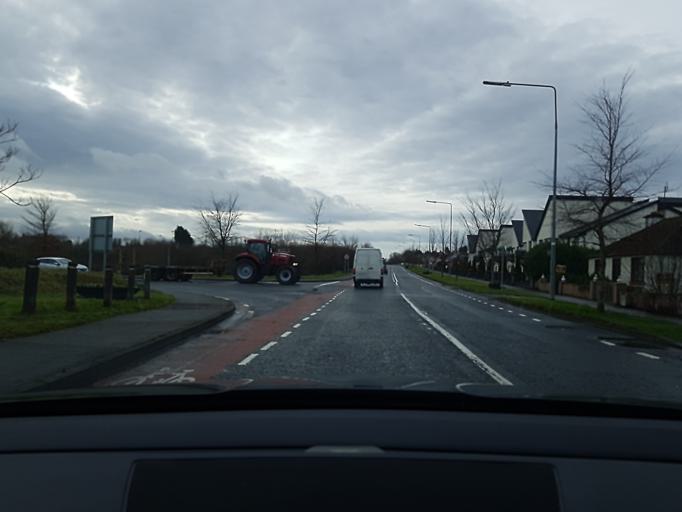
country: IE
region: Connaught
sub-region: Maigh Eo
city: Castlebar
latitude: 53.8448
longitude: -9.2895
